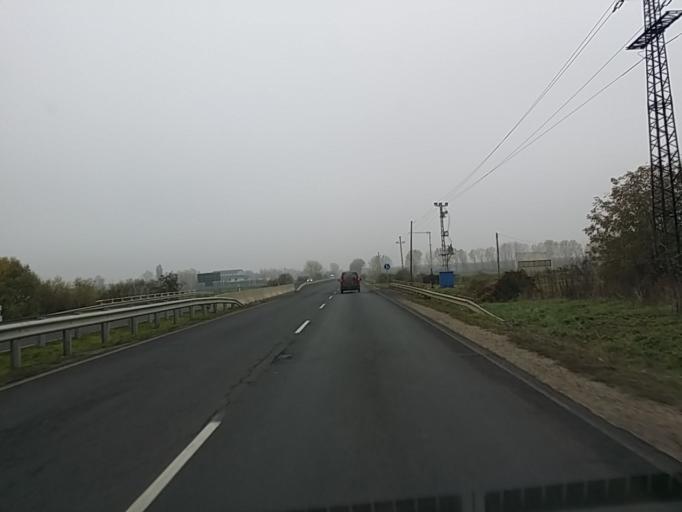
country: HU
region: Heves
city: Gyongyos
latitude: 47.7625
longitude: 19.9065
